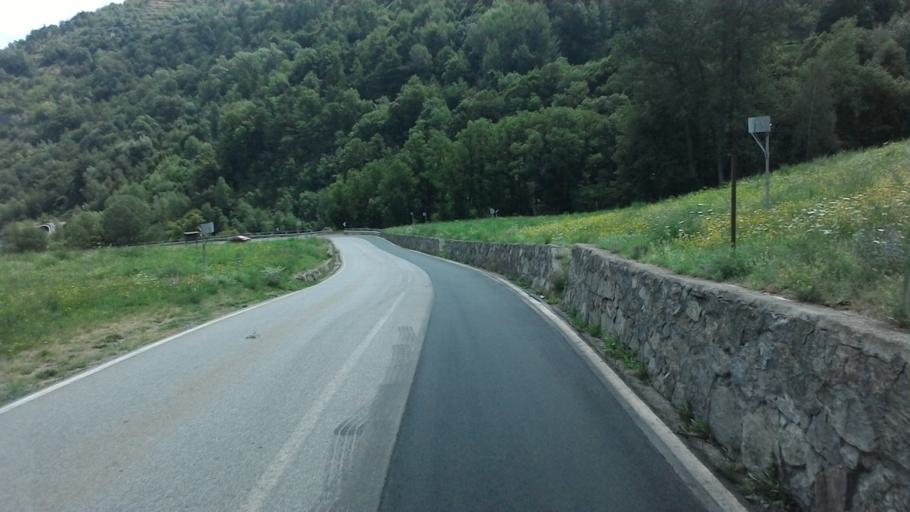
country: IT
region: Aosta Valley
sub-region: Valle d'Aosta
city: Plan d'Introd
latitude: 45.6959
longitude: 7.1933
